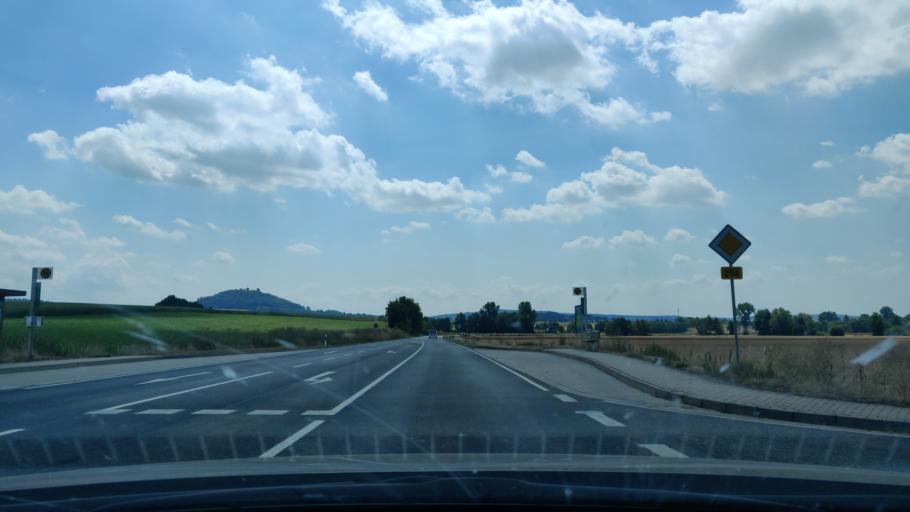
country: DE
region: Hesse
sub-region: Regierungsbezirk Kassel
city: Homberg
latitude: 51.0595
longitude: 9.3860
